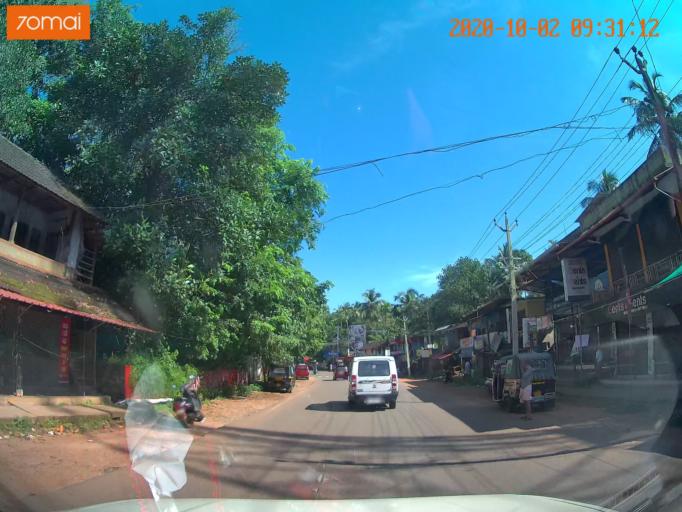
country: IN
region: Kerala
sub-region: Kozhikode
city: Nadapuram
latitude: 11.6227
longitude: 75.7612
